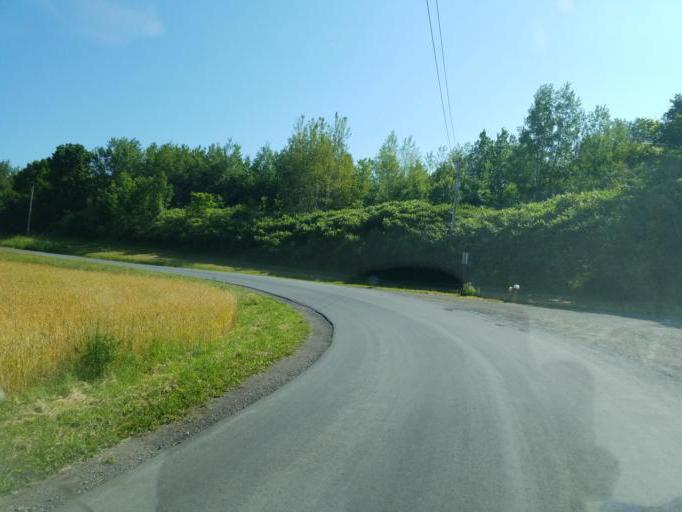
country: US
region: New York
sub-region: Wayne County
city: Clyde
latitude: 43.0553
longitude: -76.8752
